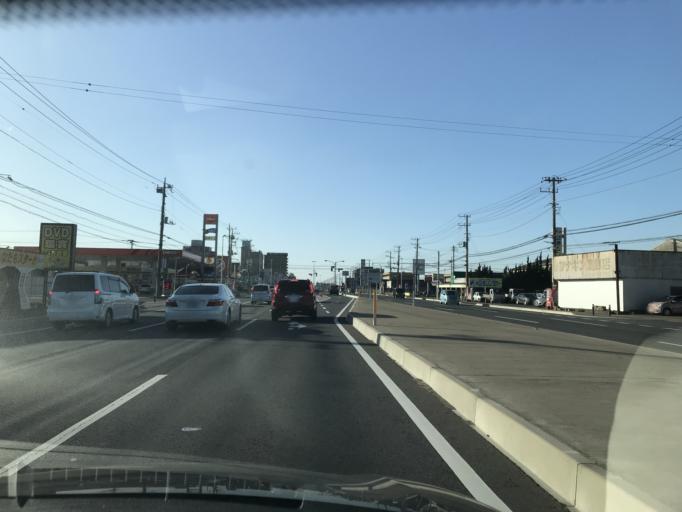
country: JP
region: Chiba
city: Omigawa
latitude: 35.8925
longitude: 140.6562
